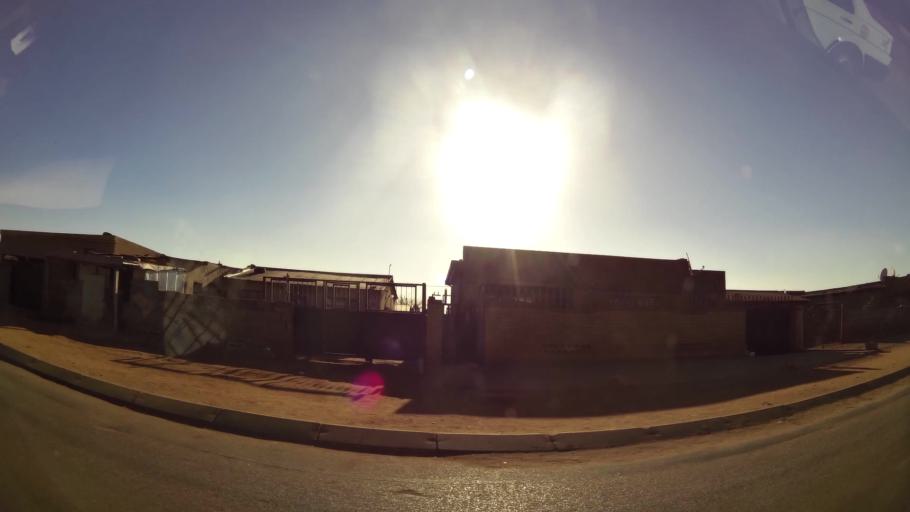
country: ZA
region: Gauteng
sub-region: Ekurhuleni Metropolitan Municipality
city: Tembisa
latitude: -26.0151
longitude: 28.2257
